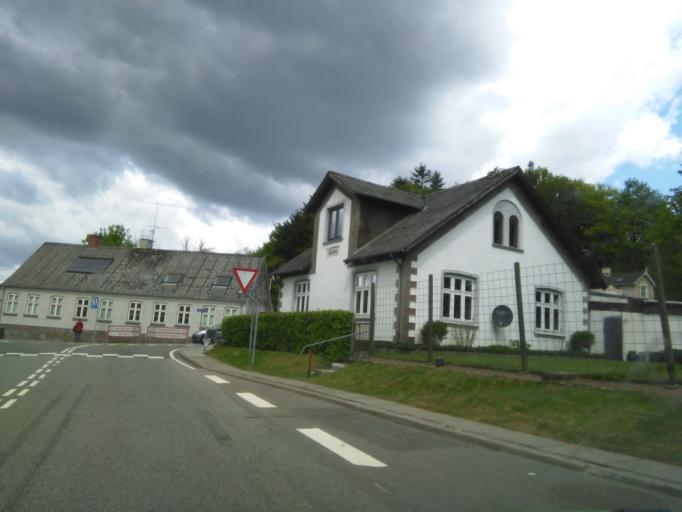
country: DK
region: Central Jutland
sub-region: Horsens Kommune
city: Braedstrup
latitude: 56.0135
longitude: 9.6980
